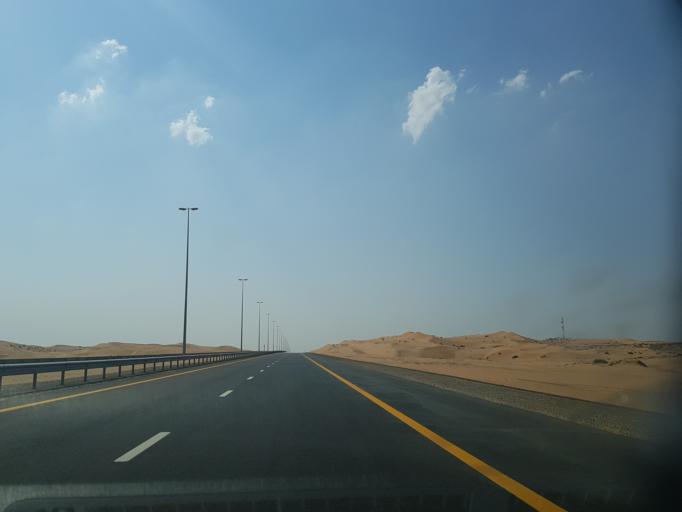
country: AE
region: Ash Shariqah
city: Adh Dhayd
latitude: 25.2579
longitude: 55.7083
